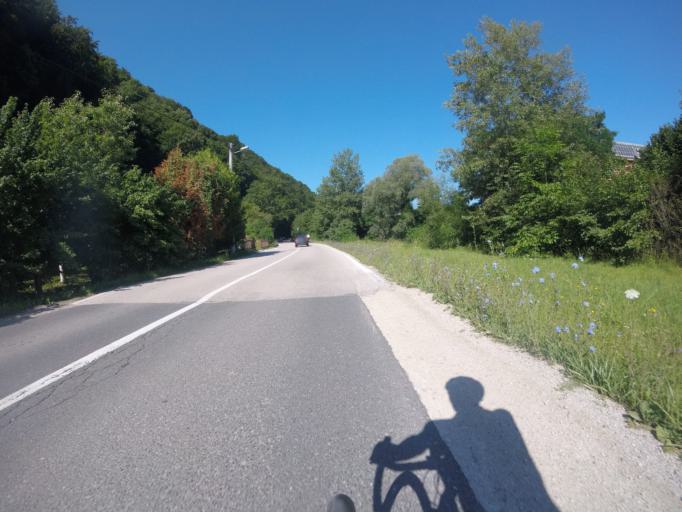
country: HR
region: Zagrebacka
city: Bregana
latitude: 45.8411
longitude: 15.6759
